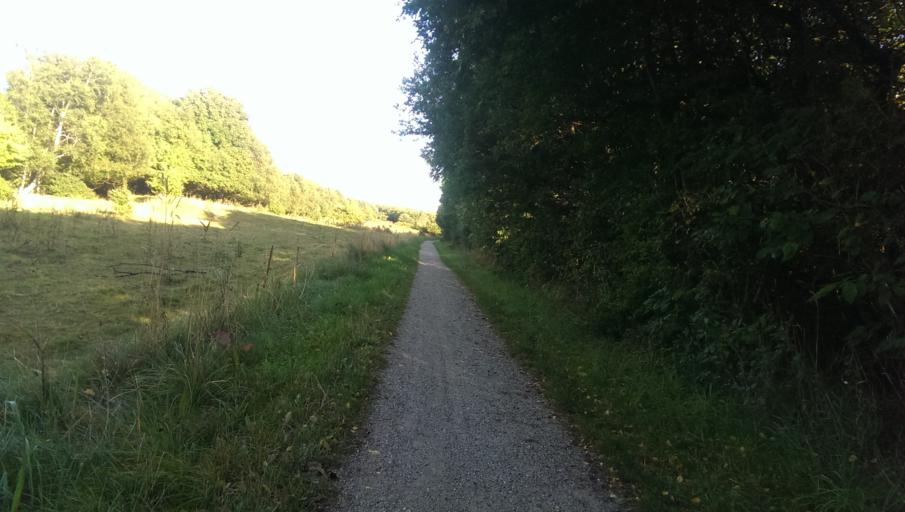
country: DK
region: South Denmark
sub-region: Esbjerg Kommune
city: Esbjerg
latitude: 55.4934
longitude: 8.4709
